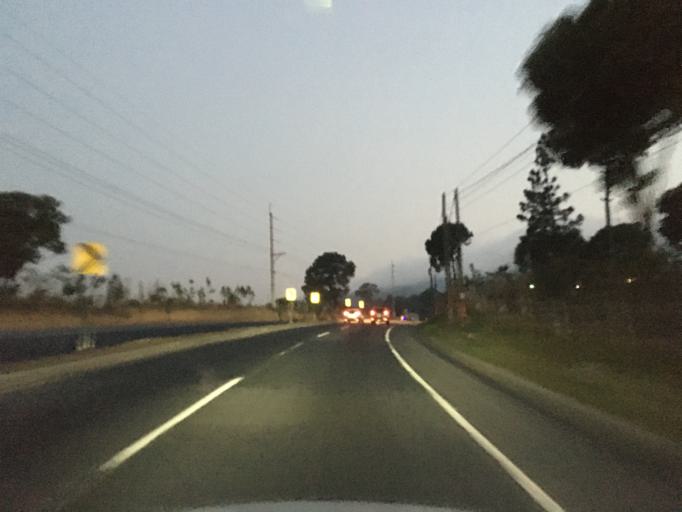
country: GT
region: Sacatepequez
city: Santo Domingo Xenacoj
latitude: 14.6565
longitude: -90.7053
